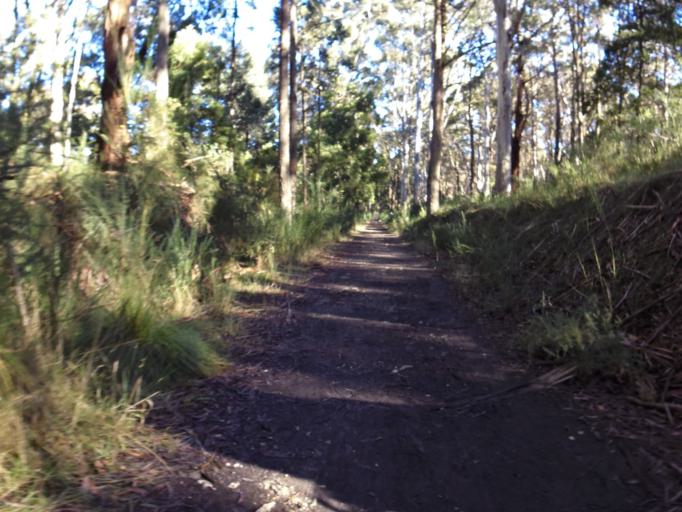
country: AU
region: Victoria
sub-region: Moorabool
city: Bacchus Marsh
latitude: -37.3877
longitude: 144.3055
